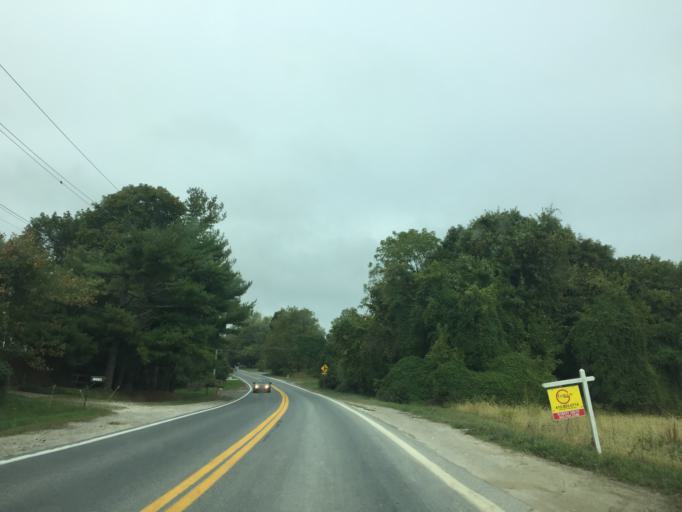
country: US
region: Maryland
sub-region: Baltimore County
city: Garrison
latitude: 39.4591
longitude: -76.7305
